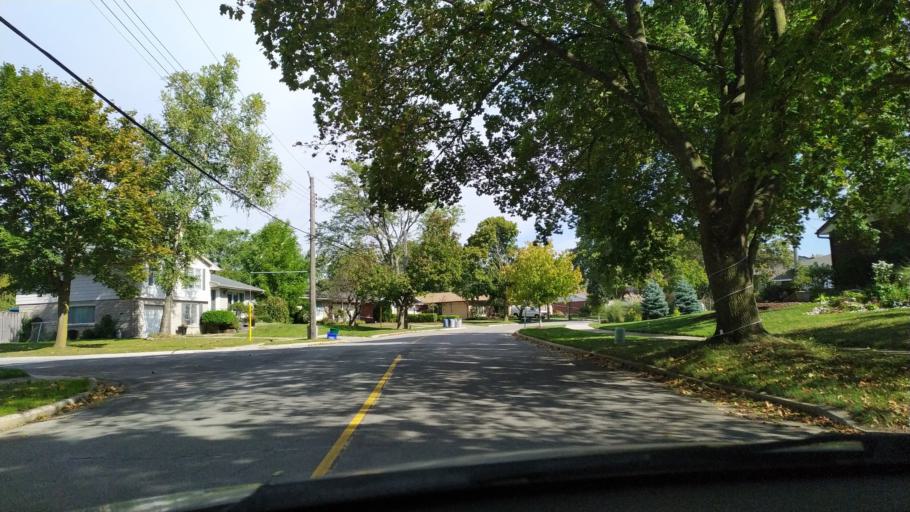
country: CA
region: Ontario
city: Kitchener
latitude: 43.4298
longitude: -80.5117
